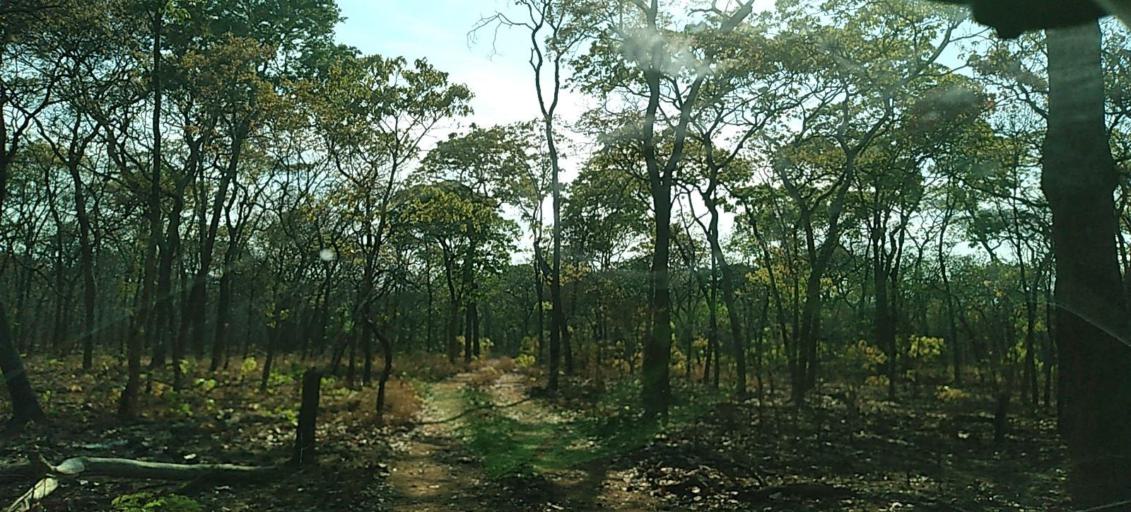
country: ZM
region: North-Western
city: Kalengwa
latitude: -13.2297
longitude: 25.0773
